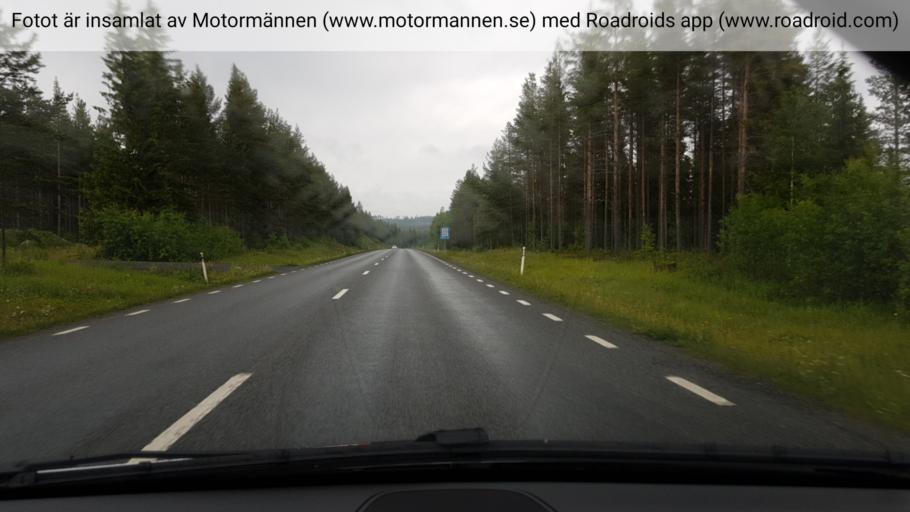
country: SE
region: Jaemtland
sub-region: OEstersunds Kommun
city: Lit
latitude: 63.3927
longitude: 14.9679
